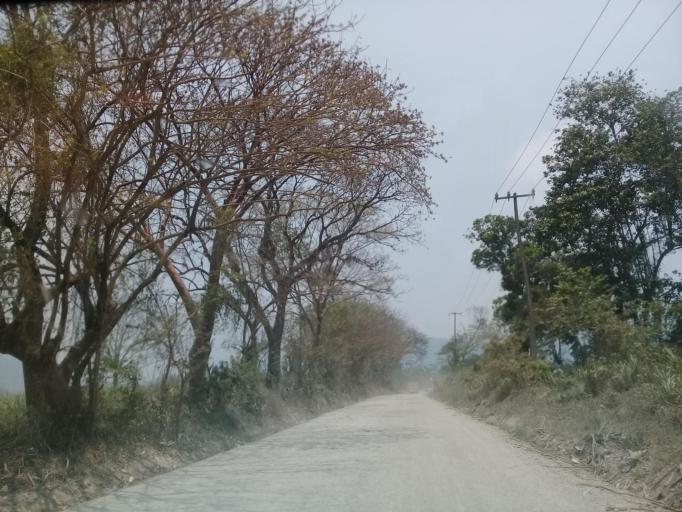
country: MX
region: Veracruz
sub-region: Tezonapa
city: Laguna Chica (Pueblo Nuevo)
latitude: 18.5690
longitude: -96.7200
